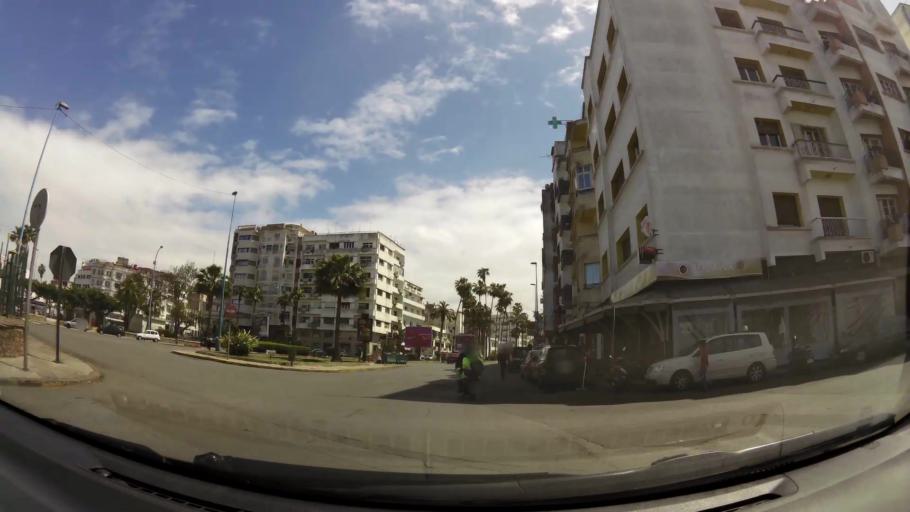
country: MA
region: Grand Casablanca
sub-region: Casablanca
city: Casablanca
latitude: 33.5986
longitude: -7.6326
